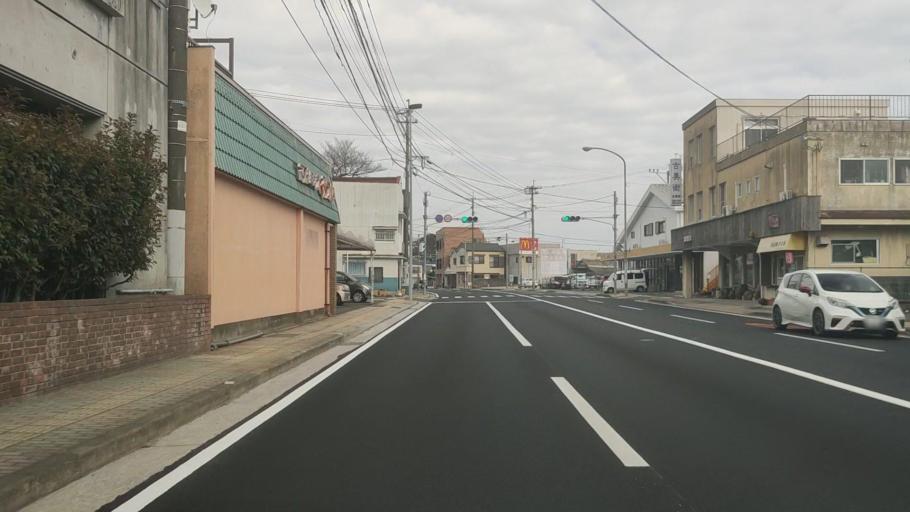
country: JP
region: Nagasaki
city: Shimabara
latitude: 32.7698
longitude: 130.3726
